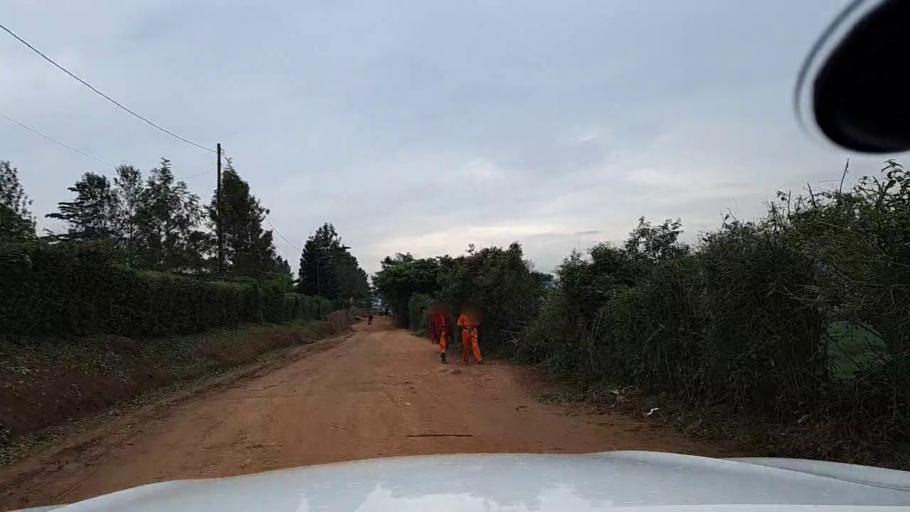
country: RW
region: Kigali
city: Kigali
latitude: -1.9602
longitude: 29.9965
